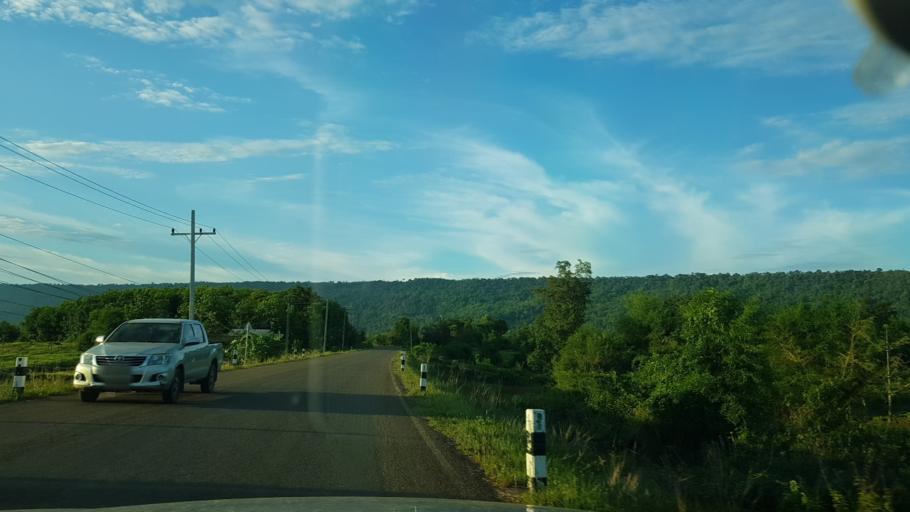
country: TH
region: Nong Khai
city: Sangkhom
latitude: 18.1048
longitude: 102.2911
